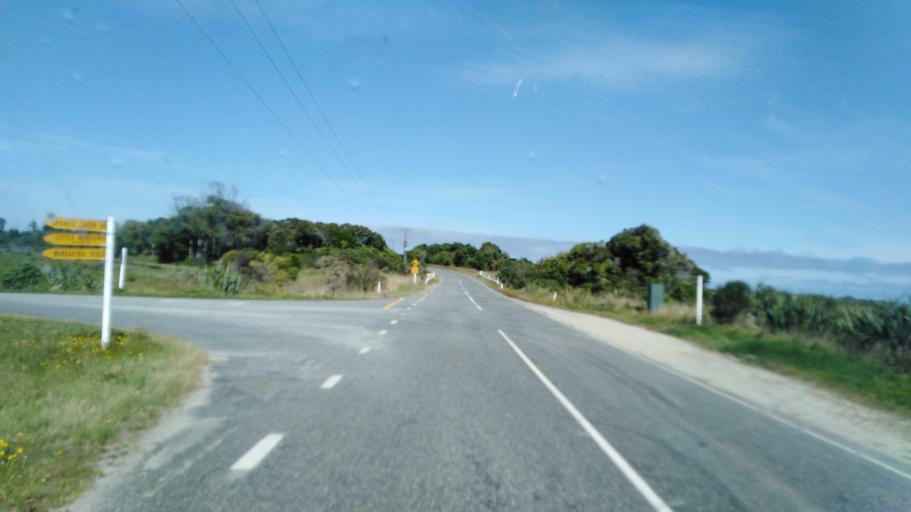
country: NZ
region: West Coast
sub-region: Buller District
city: Westport
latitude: -41.2900
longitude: 172.0990
